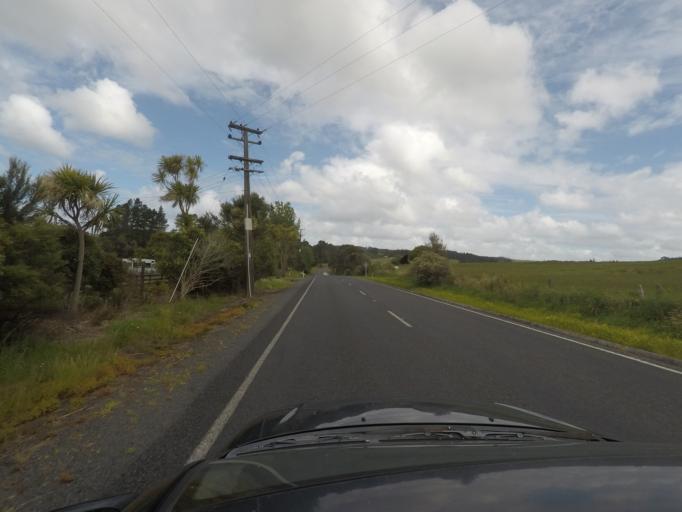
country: NZ
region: Auckland
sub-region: Auckland
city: Parakai
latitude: -36.6544
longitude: 174.5224
